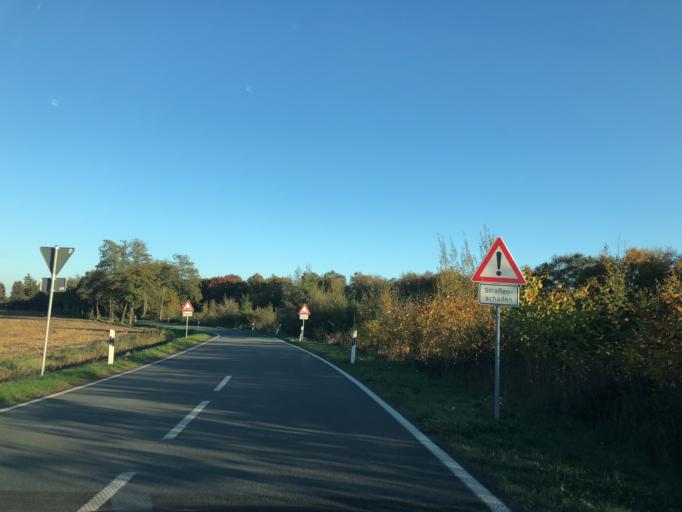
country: DE
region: Lower Saxony
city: Friesoythe
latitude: 53.0253
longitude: 7.7952
